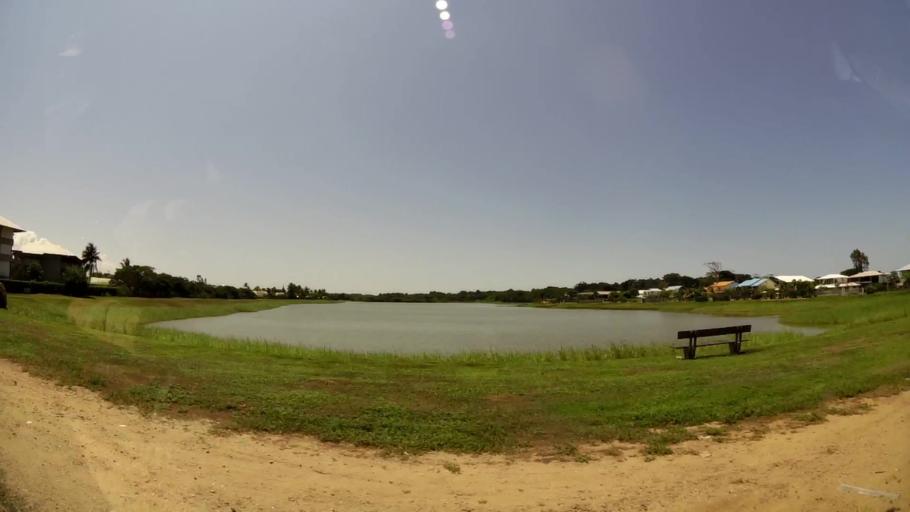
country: GF
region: Guyane
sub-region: Guyane
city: Kourou
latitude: 5.1733
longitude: -52.6563
